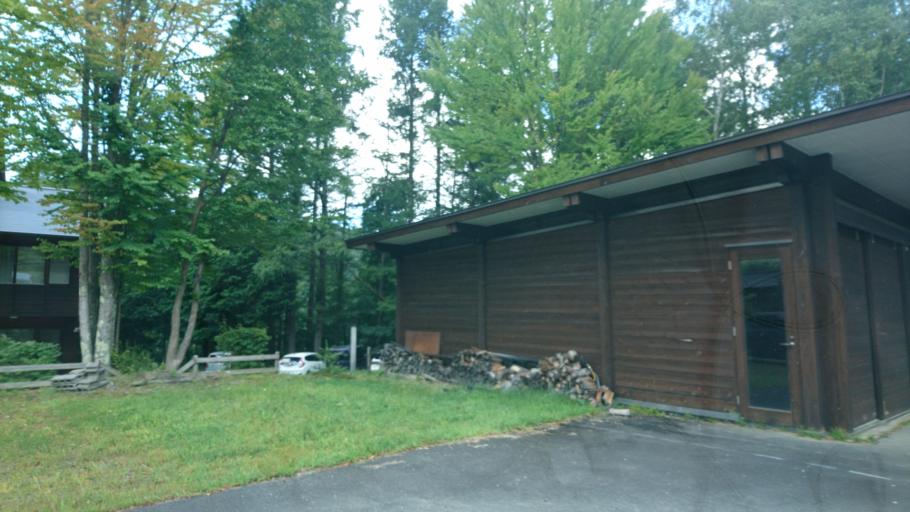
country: JP
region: Gunma
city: Omamacho-omama
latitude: 36.6035
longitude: 139.2406
